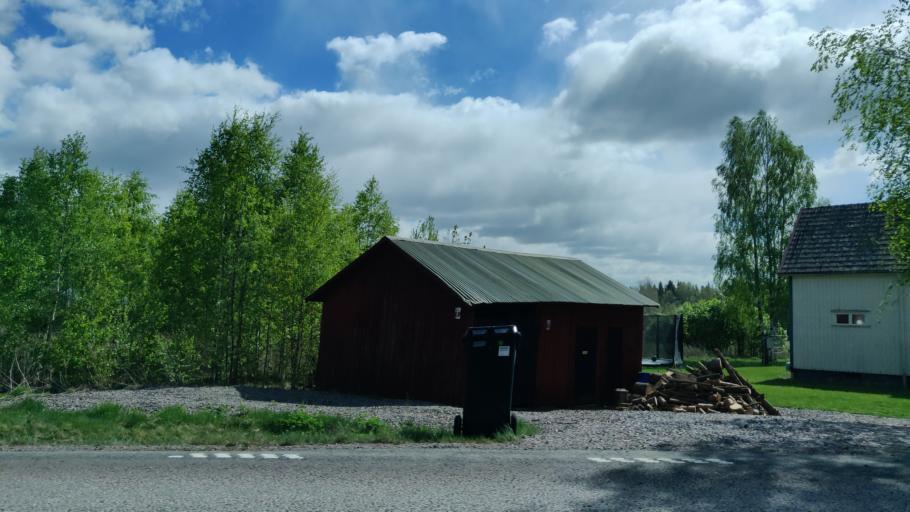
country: SE
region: Vaermland
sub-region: Karlstads Kommun
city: Molkom
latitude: 59.5482
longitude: 13.6524
